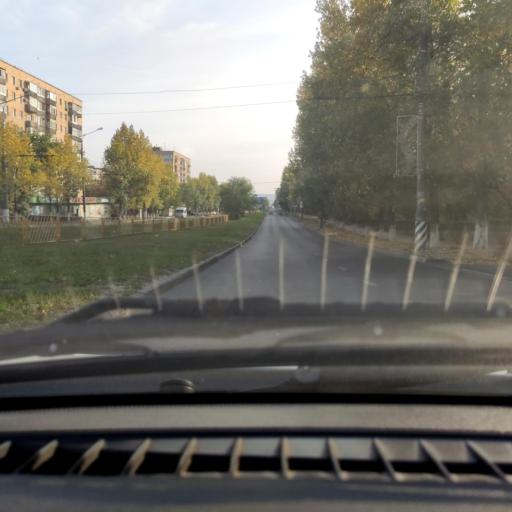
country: RU
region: Samara
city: Zhigulevsk
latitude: 53.4858
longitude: 49.4746
